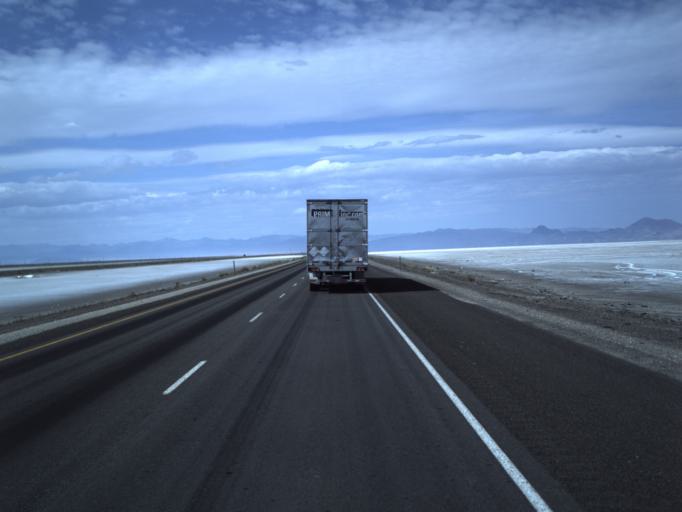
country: US
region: Utah
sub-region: Tooele County
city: Wendover
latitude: 40.7356
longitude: -113.6699
